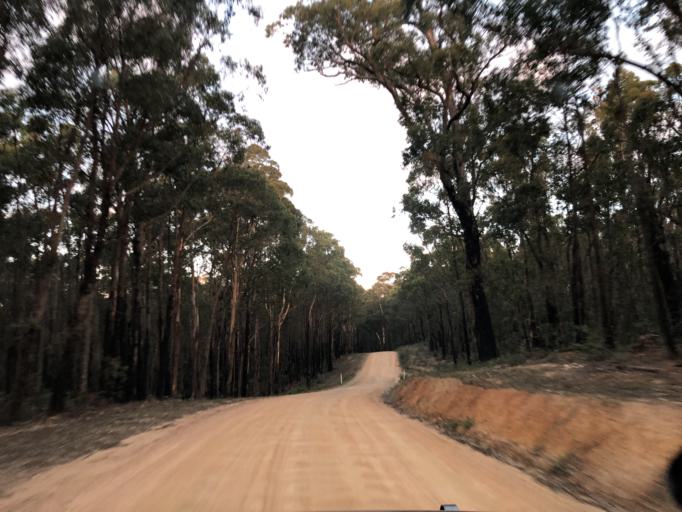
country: AU
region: Victoria
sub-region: Moorabool
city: Bacchus Marsh
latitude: -37.4731
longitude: 144.4230
